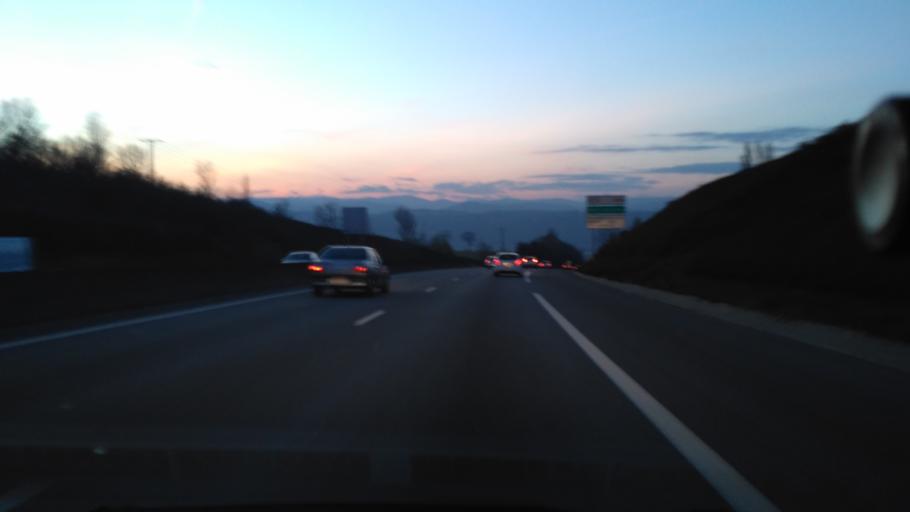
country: FR
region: Rhone-Alpes
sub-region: Departement de la Drome
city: Valence
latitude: 44.9019
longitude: 4.8969
